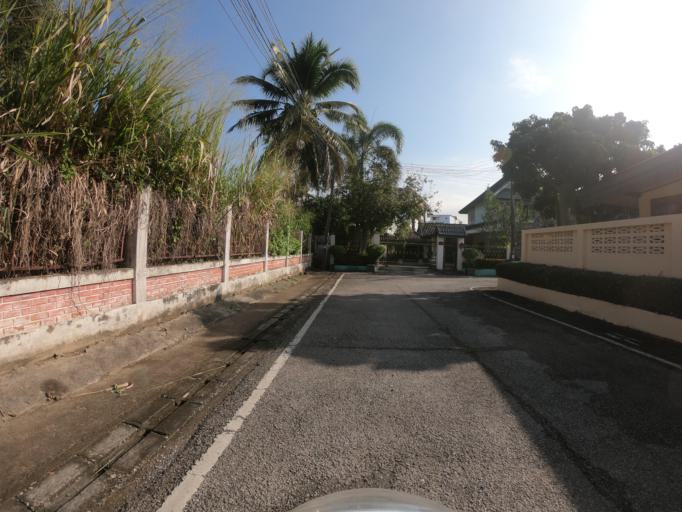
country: TH
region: Chiang Mai
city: Chiang Mai
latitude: 18.8131
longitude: 98.9677
